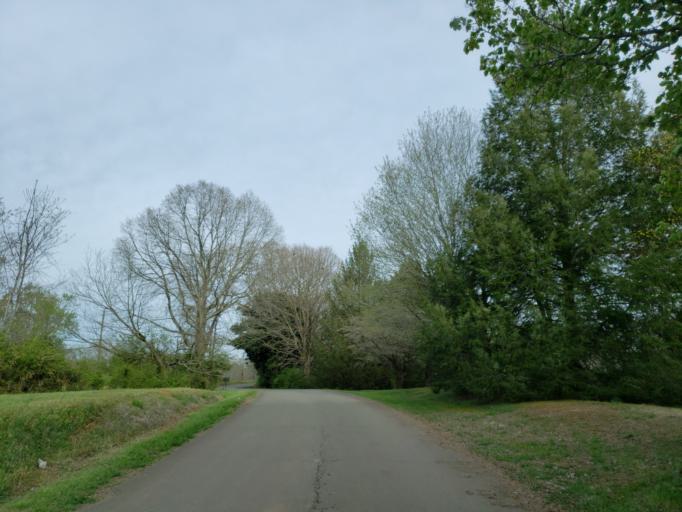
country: US
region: Georgia
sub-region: Pickens County
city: Nelson
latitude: 34.3867
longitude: -84.4325
